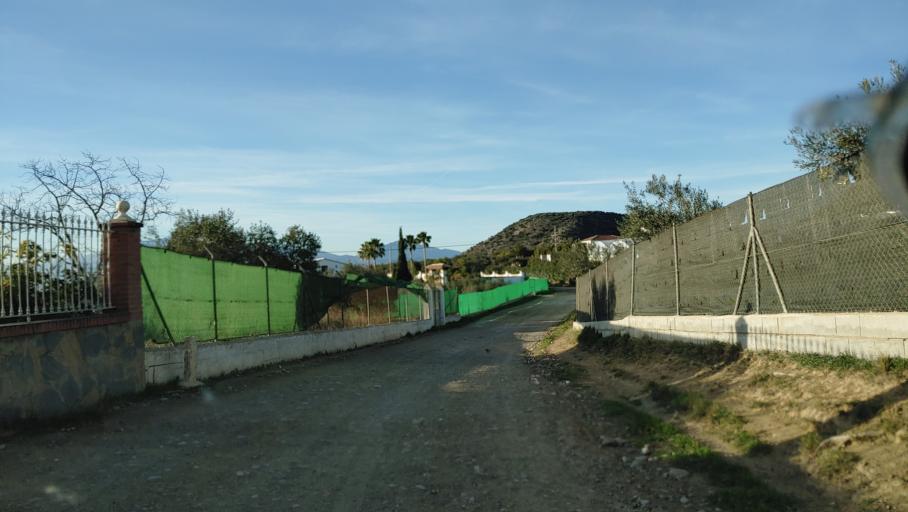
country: ES
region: Andalusia
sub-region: Provincia de Malaga
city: Cartama
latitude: 36.6852
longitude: -4.6461
